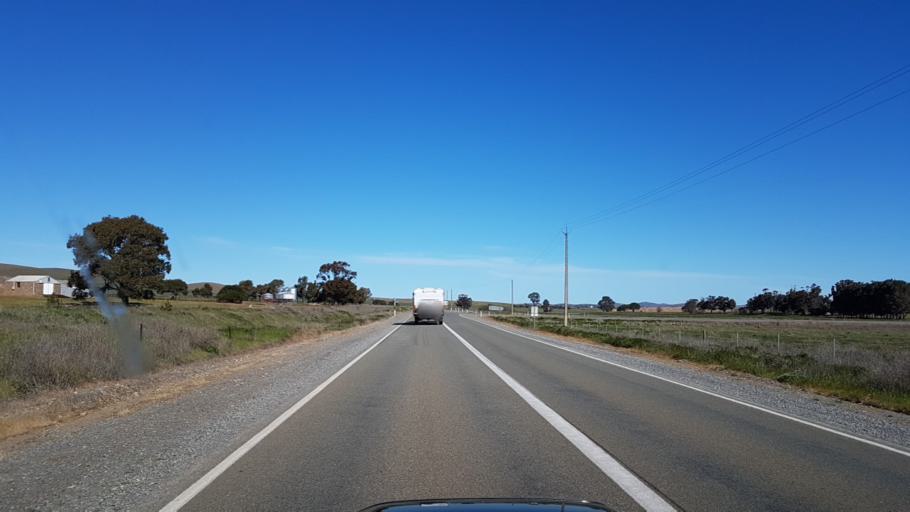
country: AU
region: South Australia
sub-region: Clare and Gilbert Valleys
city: Clare
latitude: -33.6168
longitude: 138.8977
